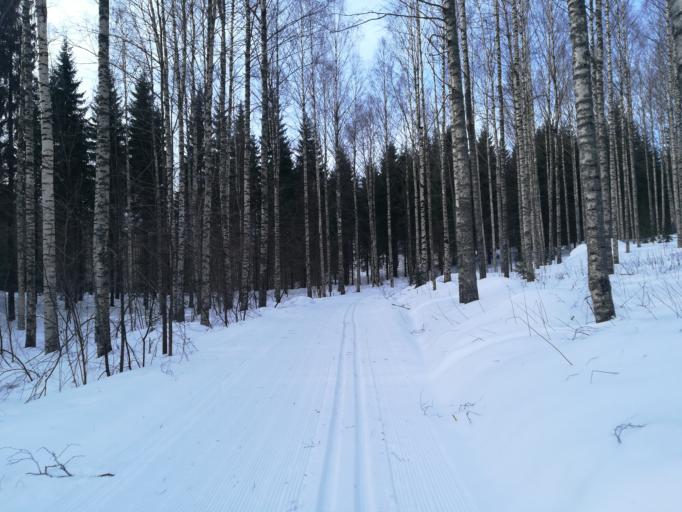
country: FI
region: Southern Savonia
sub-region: Savonlinna
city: Savonlinna
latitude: 61.8066
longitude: 29.0571
